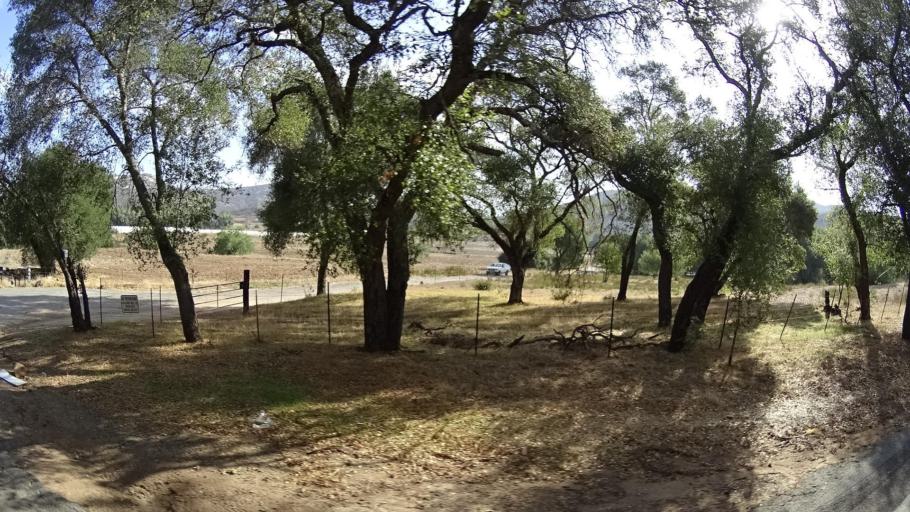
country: US
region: California
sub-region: San Diego County
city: Valley Center
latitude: 33.1758
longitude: -116.9699
